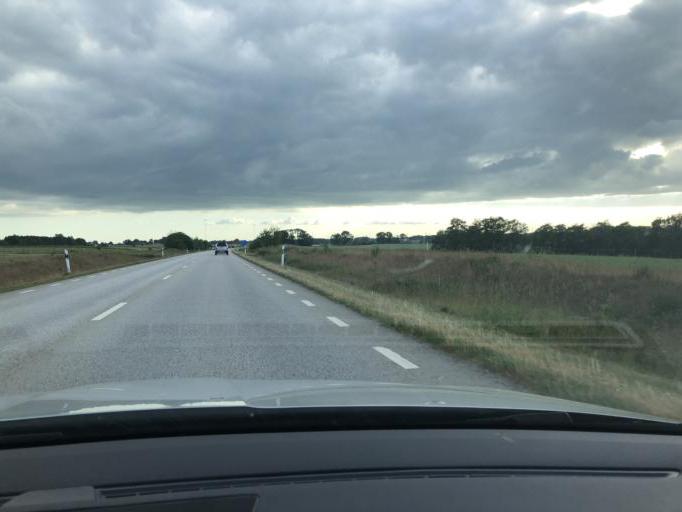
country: SE
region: Skane
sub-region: Simrishamns Kommun
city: Simrishamn
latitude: 55.5399
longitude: 14.3246
